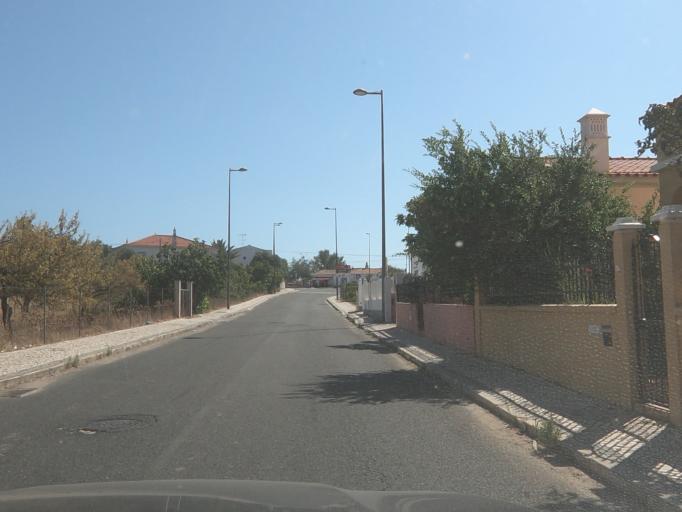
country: PT
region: Faro
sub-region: Faro
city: Santa Barbara de Nexe
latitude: 37.0874
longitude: -7.9891
